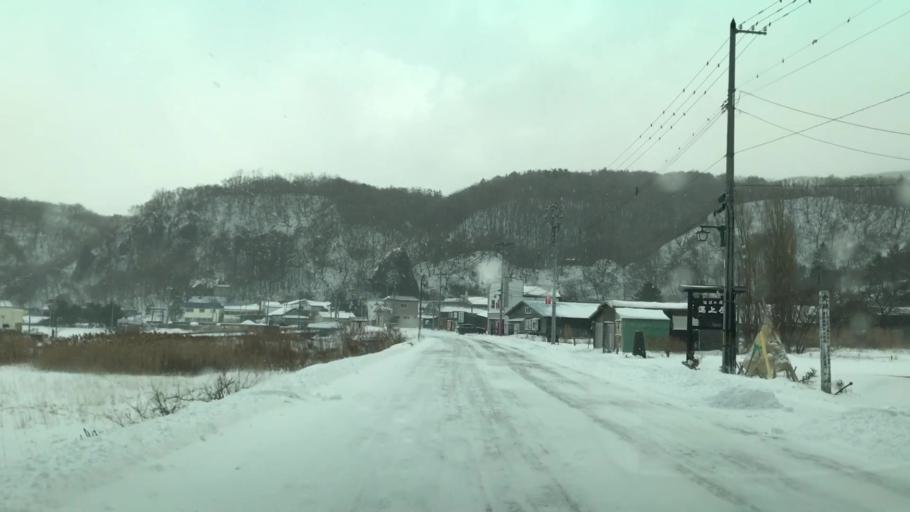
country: JP
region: Hokkaido
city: Iwanai
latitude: 43.3308
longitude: 140.3947
